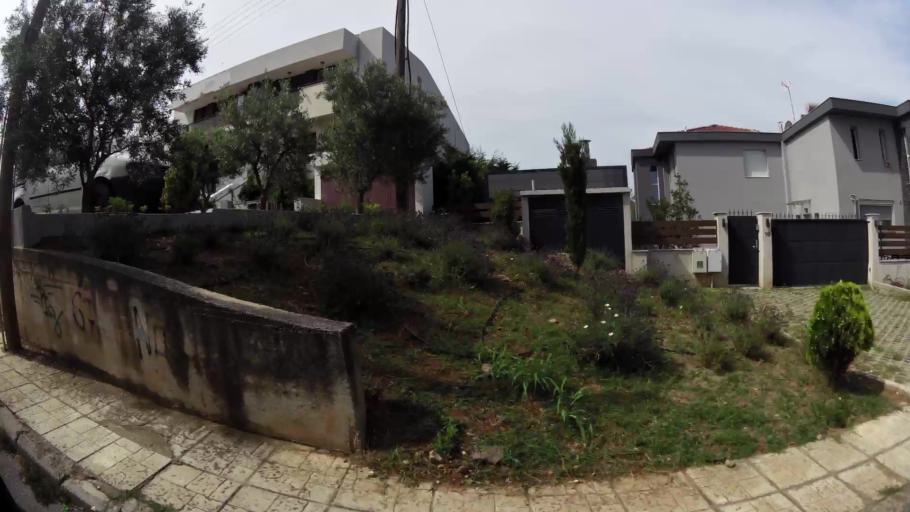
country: GR
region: Central Macedonia
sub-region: Nomos Thessalonikis
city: Panorama
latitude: 40.5795
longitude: 23.0114
